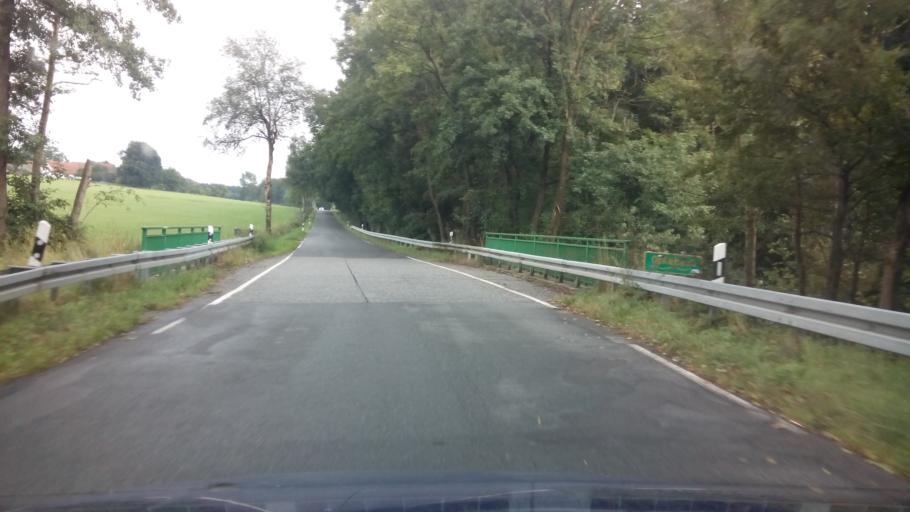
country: DE
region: Lower Saxony
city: Bad Essen
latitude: 52.2939
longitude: 8.3275
